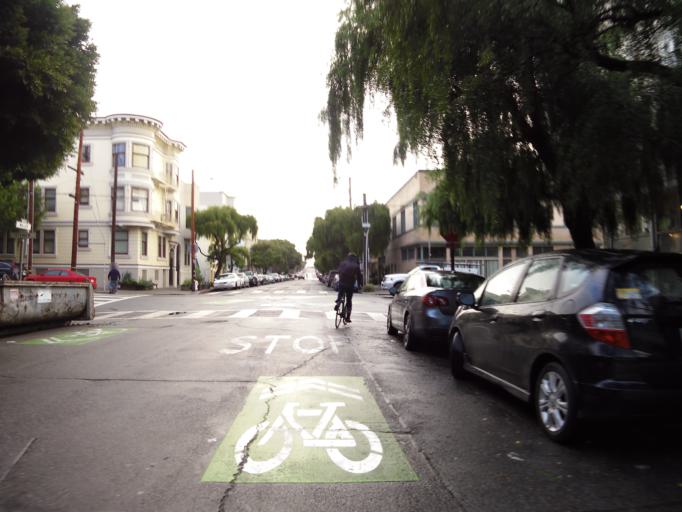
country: US
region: California
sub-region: San Francisco County
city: San Francisco
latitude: 37.7709
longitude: -122.4322
